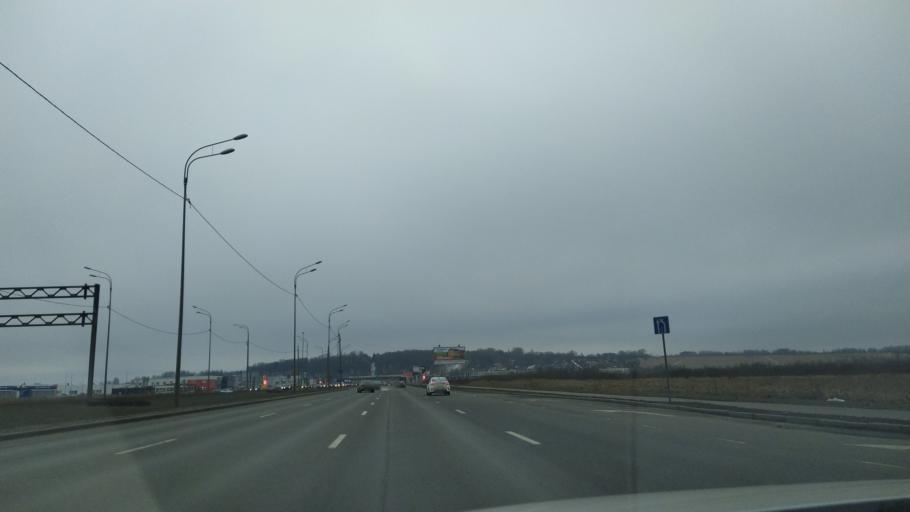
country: RU
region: St.-Petersburg
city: Aleksandrovskaya
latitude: 59.7871
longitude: 30.3247
